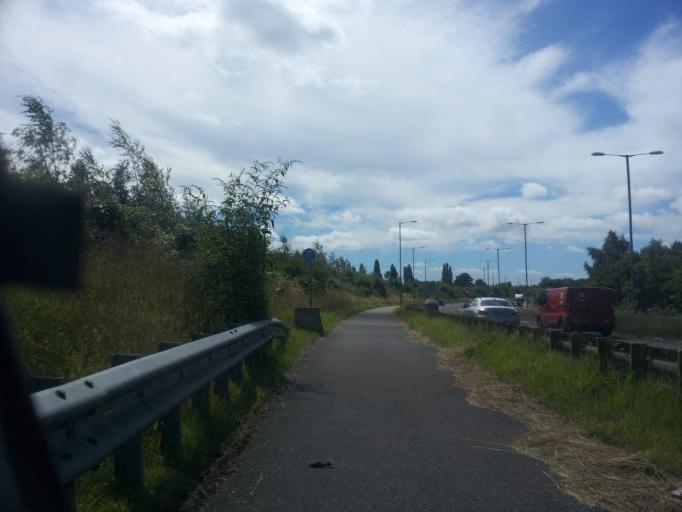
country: GB
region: England
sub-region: Kent
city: Larkfield
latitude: 51.2911
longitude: 0.4200
